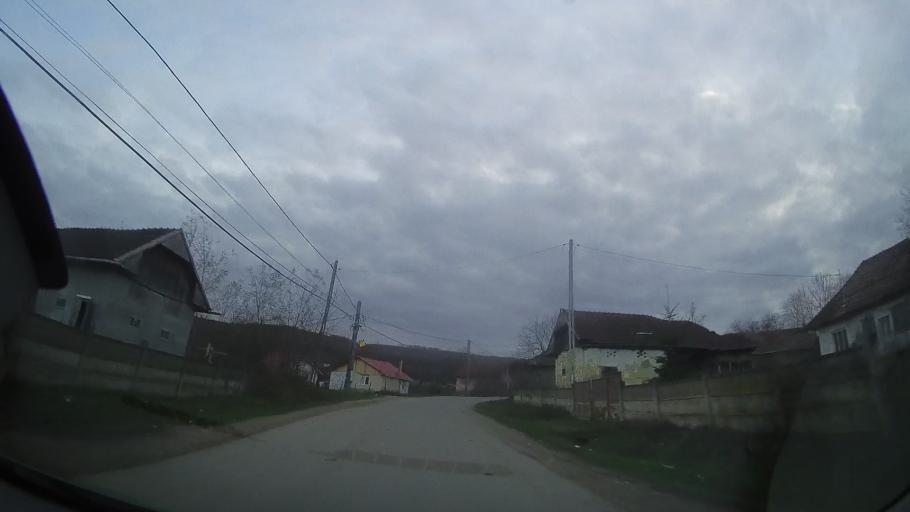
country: RO
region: Cluj
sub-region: Comuna Palatca
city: Palatca
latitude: 46.8382
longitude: 23.9834
